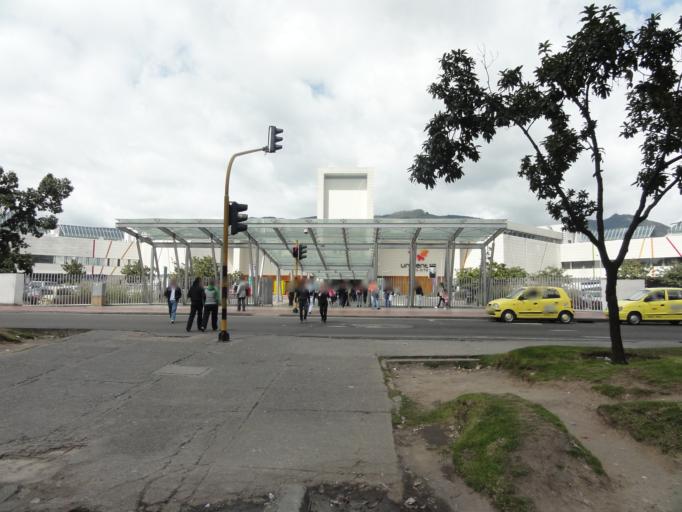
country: CO
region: Bogota D.C.
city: Barrio San Luis
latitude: 4.7023
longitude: -74.0429
